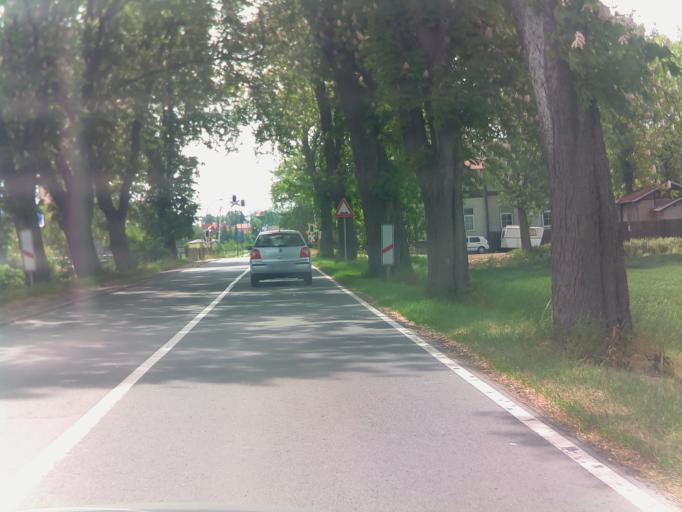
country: DE
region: Saxony-Anhalt
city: Hedersleben
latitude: 51.8463
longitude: 11.2506
